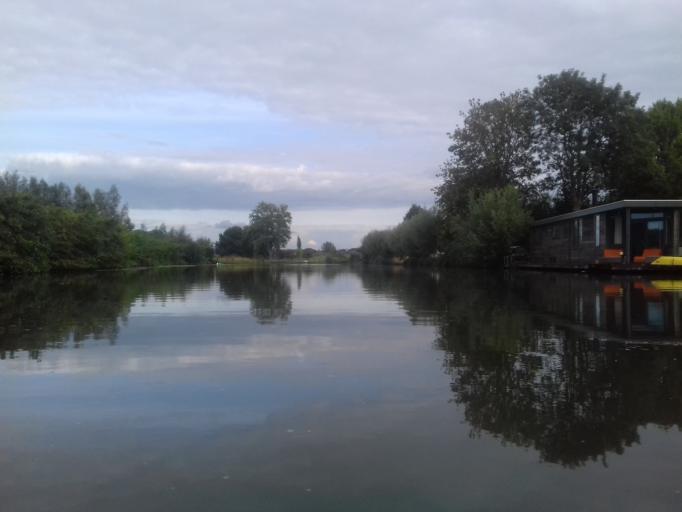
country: NL
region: Gelderland
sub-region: Gemeente Culemborg
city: Culemborg
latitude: 51.8787
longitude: 5.1915
